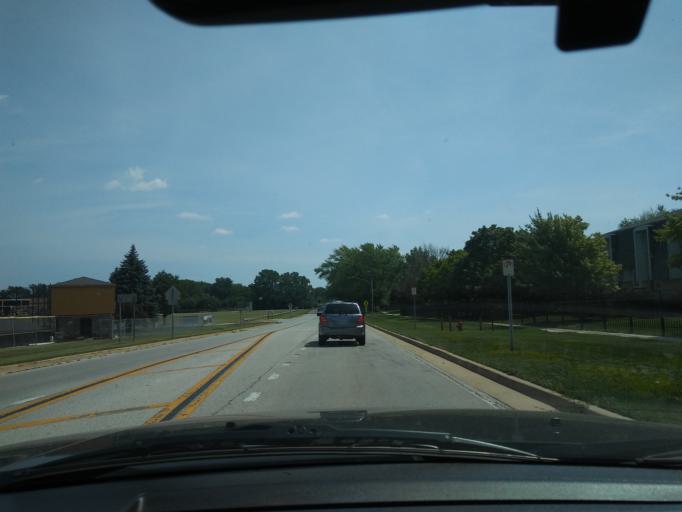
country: US
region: Illinois
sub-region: Cook County
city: Oak Forest
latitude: 41.6169
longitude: -87.7565
